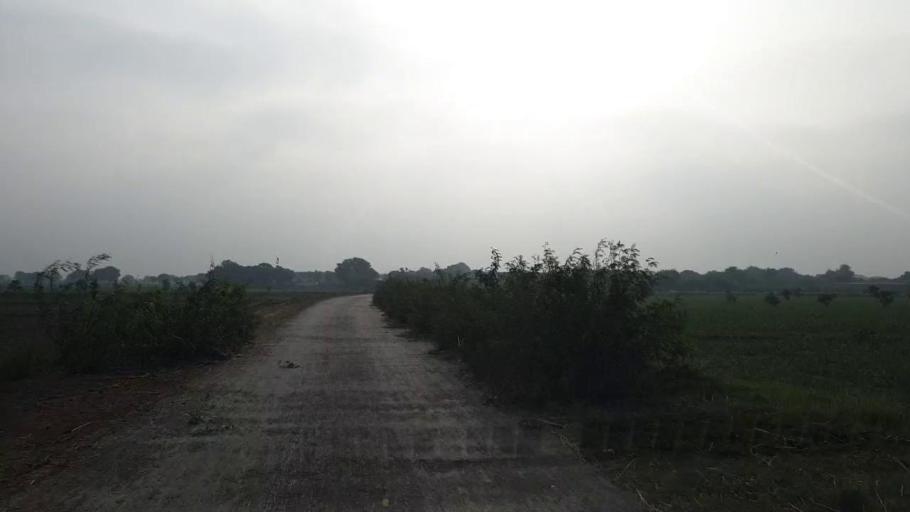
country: PK
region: Sindh
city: Tando Muhammad Khan
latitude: 25.1683
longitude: 68.6100
